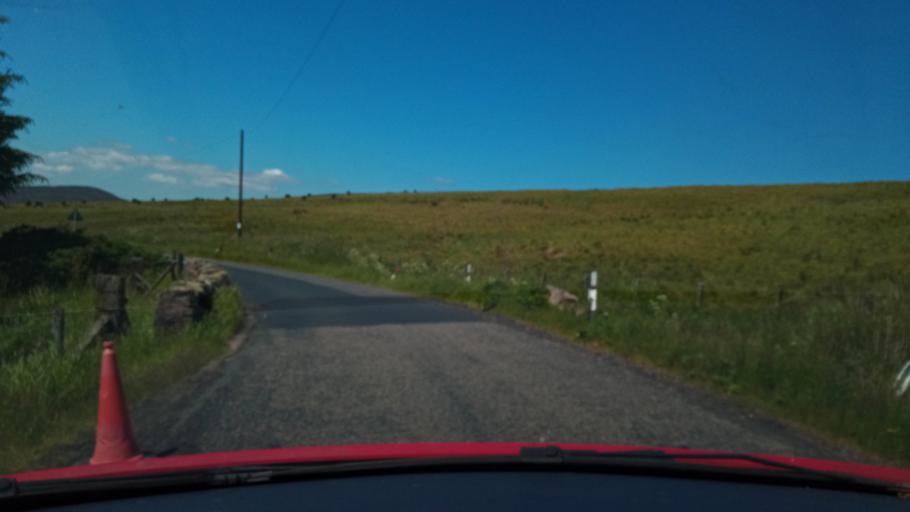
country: GB
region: Scotland
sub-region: The Scottish Borders
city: Duns
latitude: 55.7817
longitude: -2.4260
